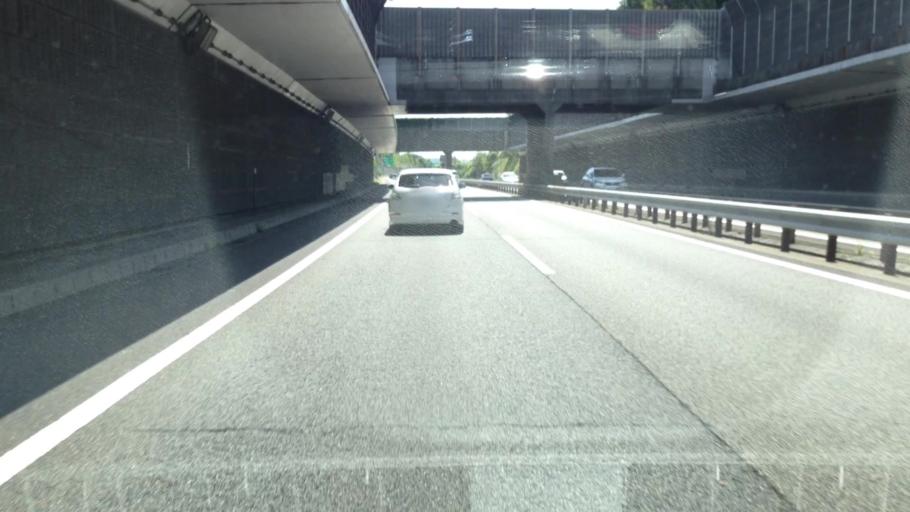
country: JP
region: Kanagawa
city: Yokohama
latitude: 35.4332
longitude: 139.5819
